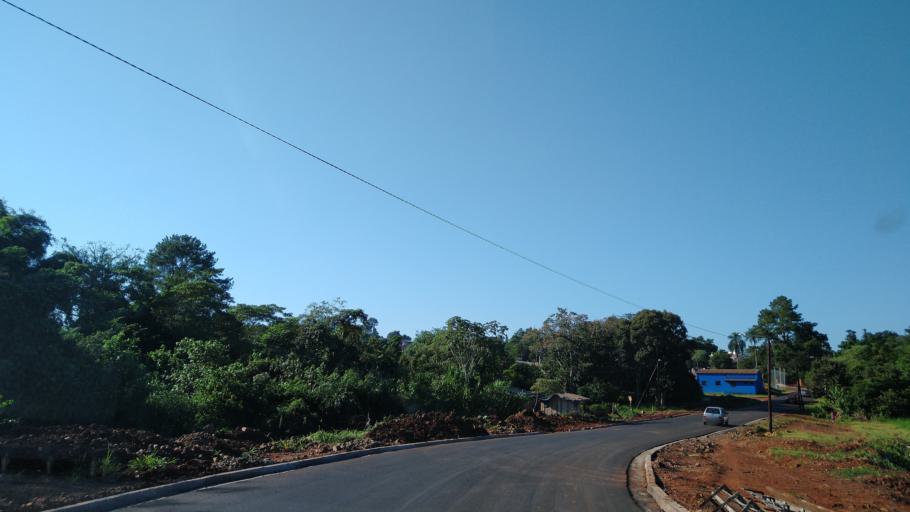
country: AR
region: Misiones
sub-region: Departamento de Montecarlo
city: Montecarlo
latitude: -26.5626
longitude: -54.7717
